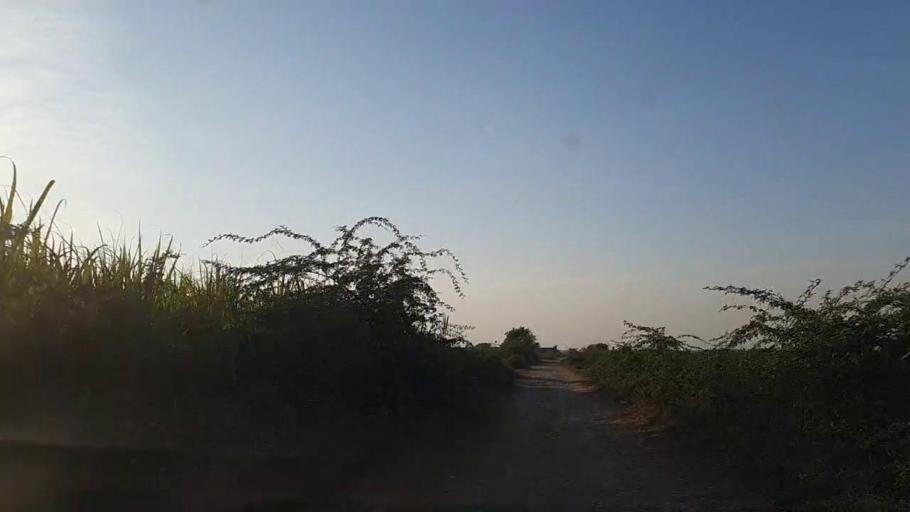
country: PK
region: Sindh
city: Mirpur Batoro
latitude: 24.6834
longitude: 68.2110
